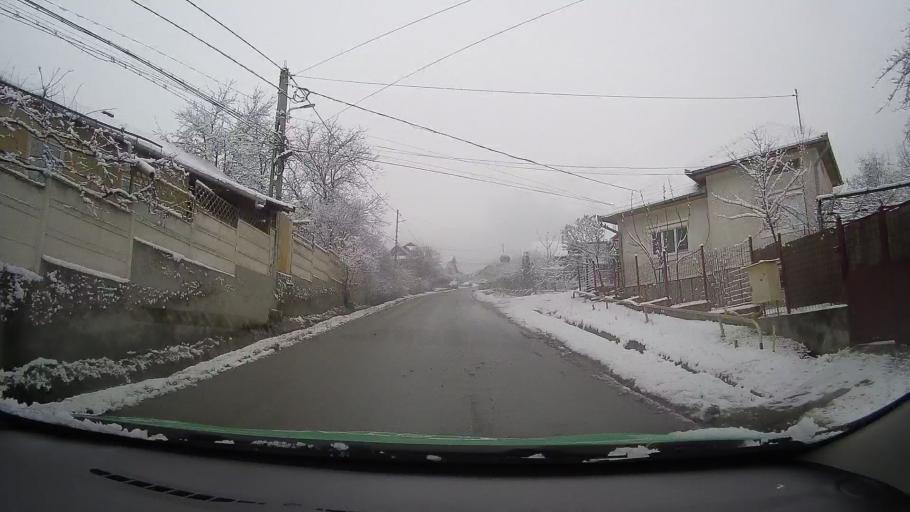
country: RO
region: Hunedoara
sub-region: Municipiul Deva
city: Deva
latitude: 45.8708
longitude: 22.8961
